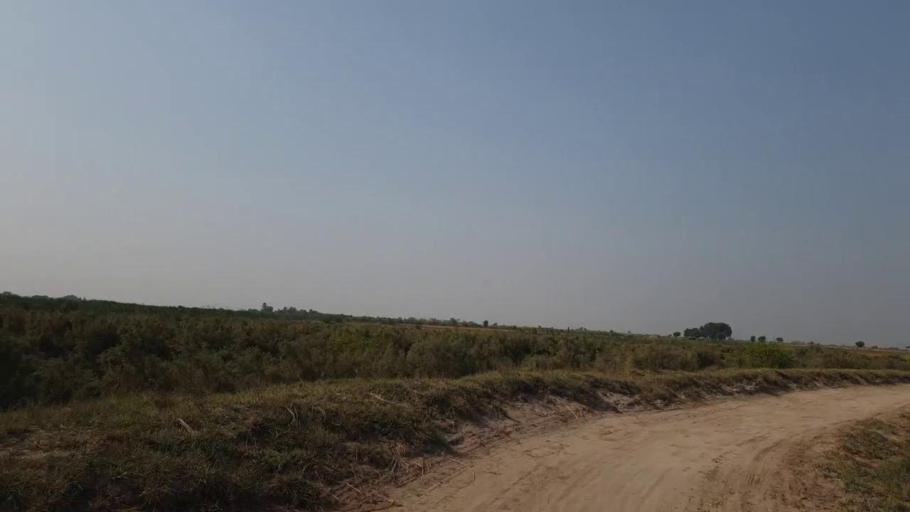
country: PK
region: Sindh
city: Bulri
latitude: 24.9465
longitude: 68.3809
